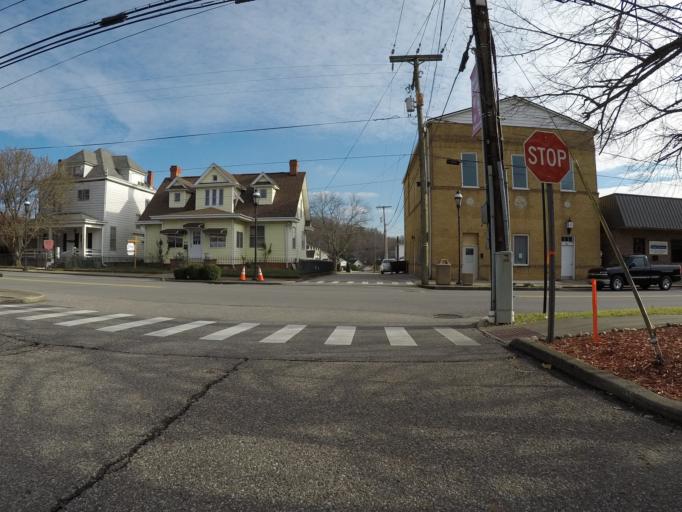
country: US
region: West Virginia
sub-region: Cabell County
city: Barboursville
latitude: 38.4088
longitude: -82.2956
